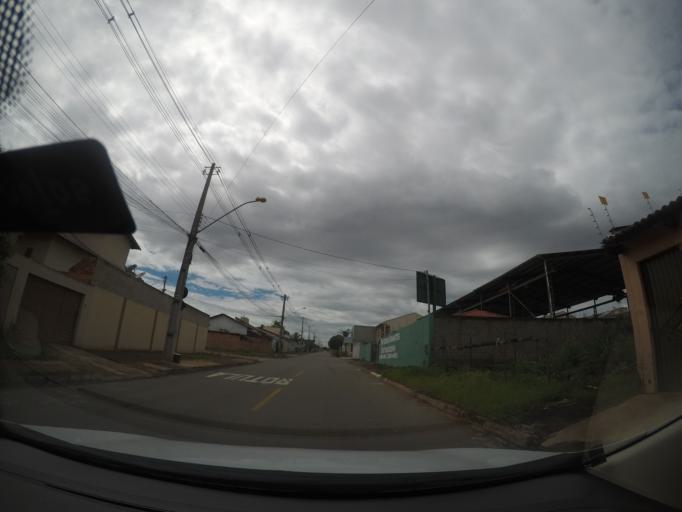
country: BR
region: Goias
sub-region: Goiania
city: Goiania
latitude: -16.7276
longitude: -49.3441
